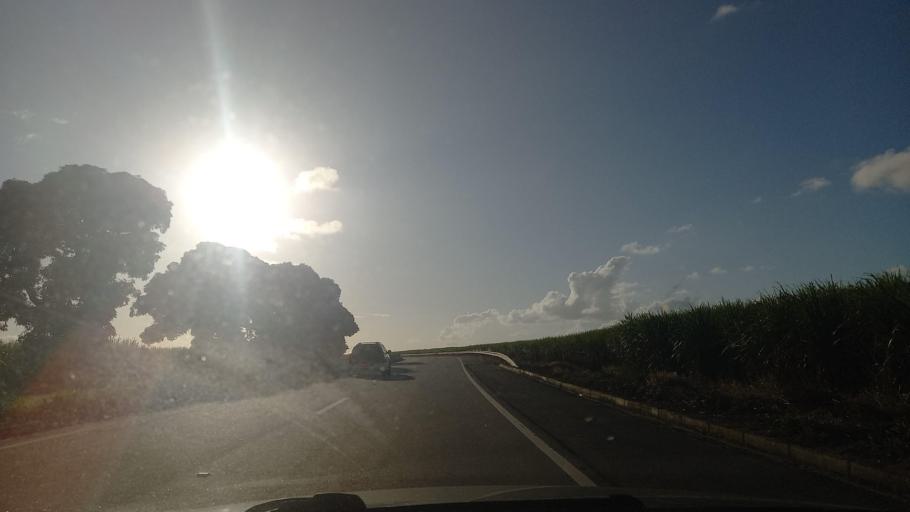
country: BR
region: Alagoas
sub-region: Campo Alegre
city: Campo Alegre
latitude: -9.8053
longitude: -36.2635
